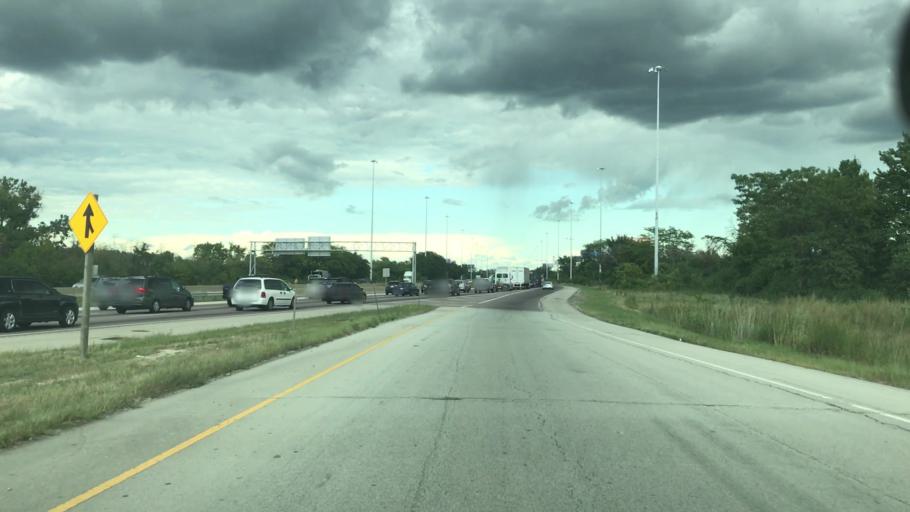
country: US
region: Illinois
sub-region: Cook County
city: Summit
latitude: 41.8000
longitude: -87.7971
